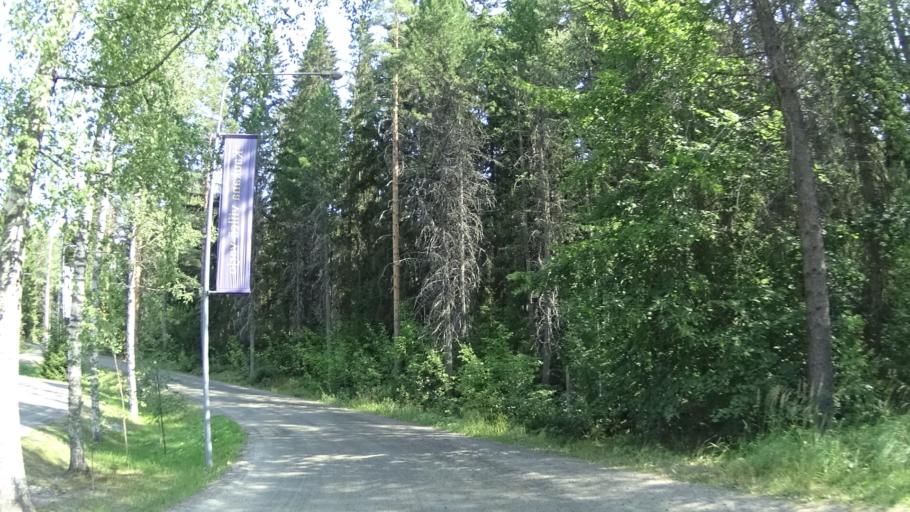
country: FI
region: Pirkanmaa
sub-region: Ylae-Pirkanmaa
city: Maenttae
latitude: 62.0279
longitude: 24.5792
